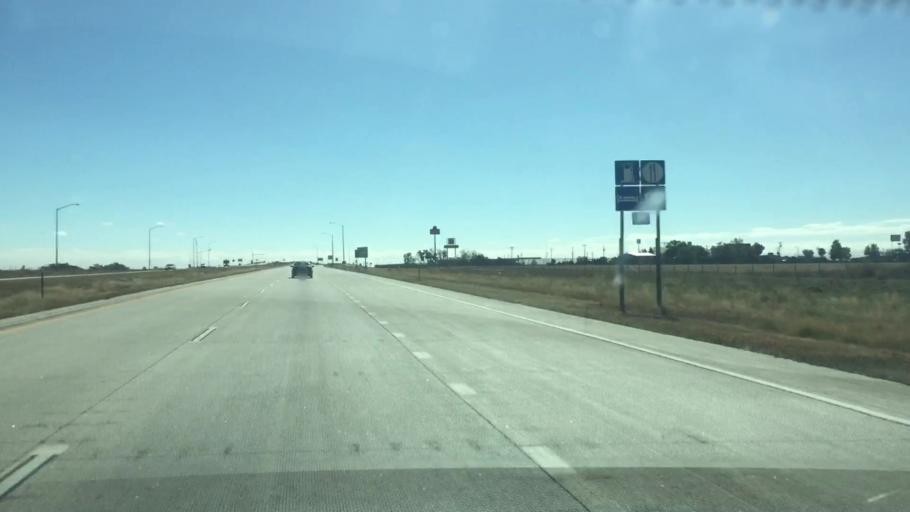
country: US
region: Colorado
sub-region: Lincoln County
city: Limon
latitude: 39.2693
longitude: -103.6759
